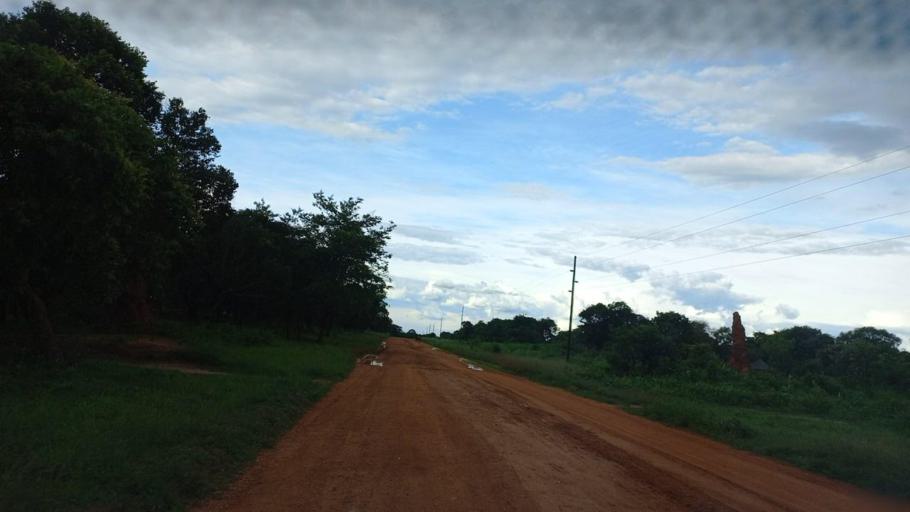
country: ZM
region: North-Western
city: Mwinilunga
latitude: -11.7723
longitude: 24.4067
